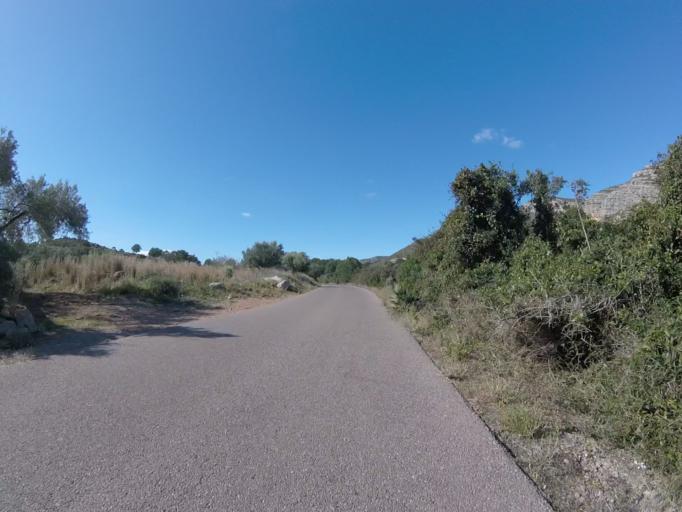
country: ES
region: Valencia
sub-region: Provincia de Castello
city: Orpesa/Oropesa del Mar
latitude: 40.0886
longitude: 0.1259
